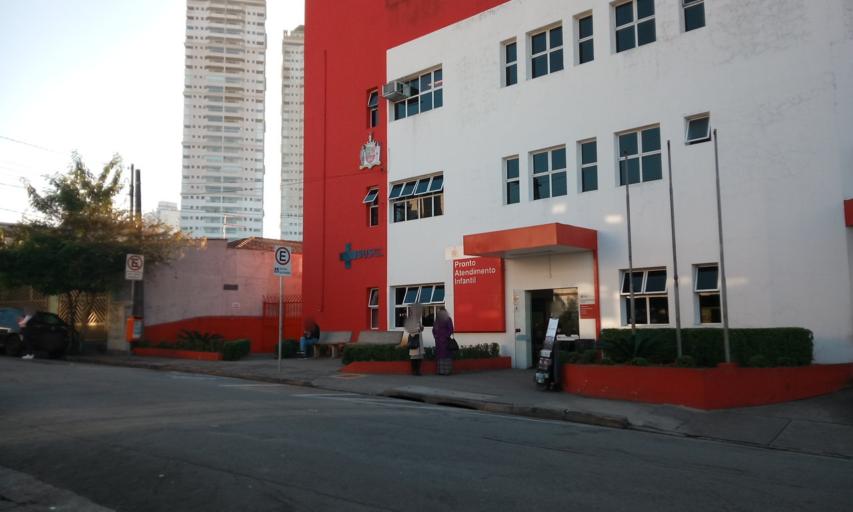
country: BR
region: Sao Paulo
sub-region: Sao Bernardo Do Campo
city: Sao Bernardo do Campo
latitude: -23.7155
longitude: -46.5558
